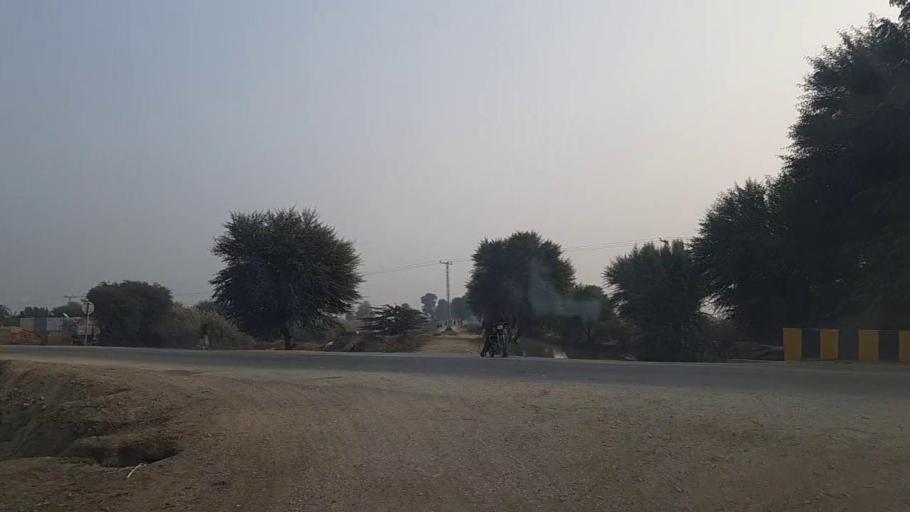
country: PK
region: Sindh
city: Sinjhoro
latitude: 26.1157
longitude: 68.8046
